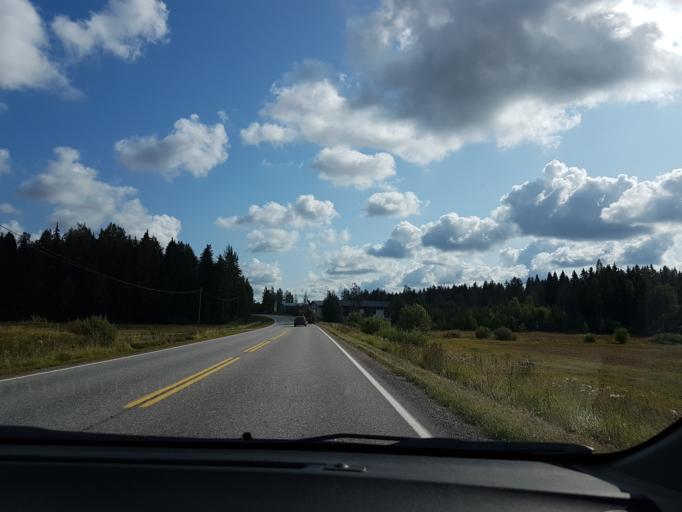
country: FI
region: Uusimaa
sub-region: Helsinki
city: Pornainen
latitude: 60.4737
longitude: 25.3100
